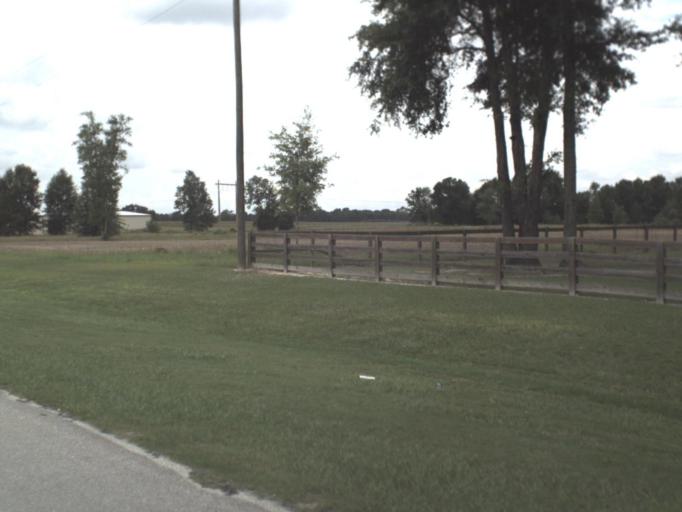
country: US
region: Florida
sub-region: Alachua County
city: Newberry
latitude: 29.7075
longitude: -82.6071
